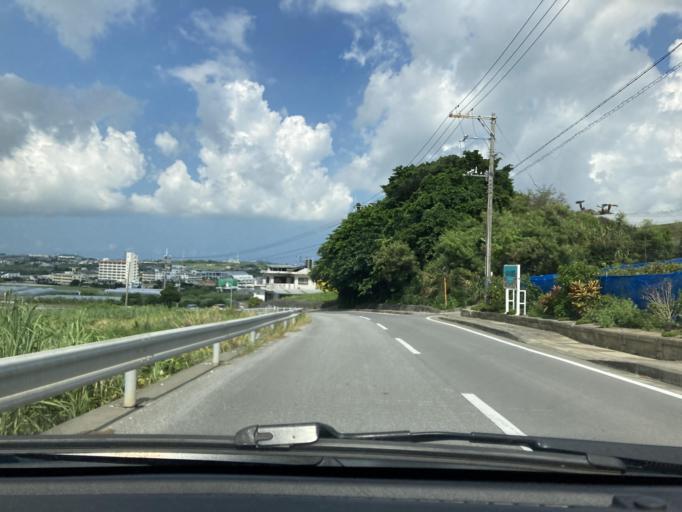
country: JP
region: Okinawa
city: Tomigusuku
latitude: 26.1495
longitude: 127.7582
